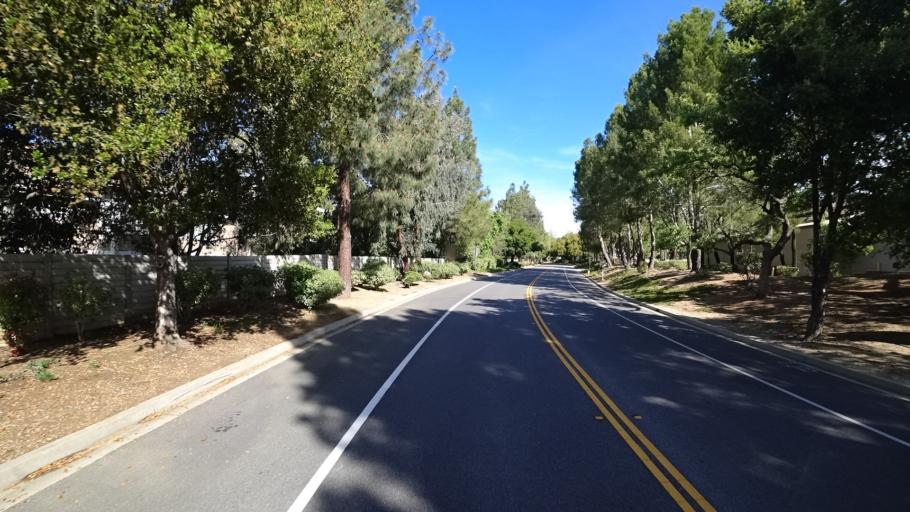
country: US
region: California
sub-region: Ventura County
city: Oak Park
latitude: 34.1836
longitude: -118.7888
